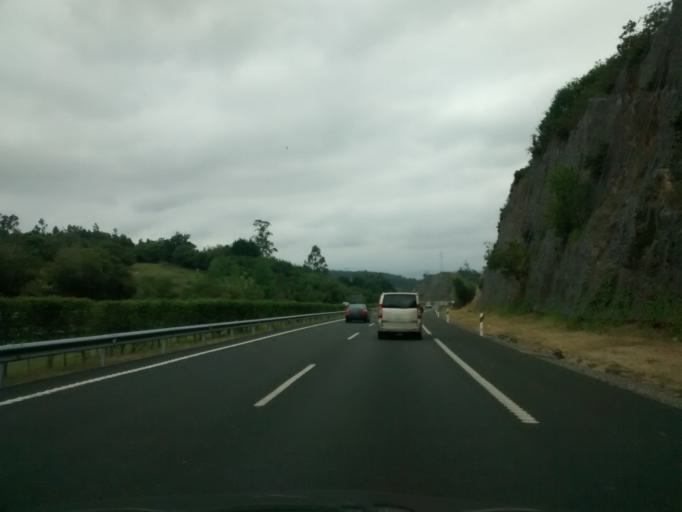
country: ES
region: Cantabria
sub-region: Provincia de Cantabria
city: Reocin
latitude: 43.3403
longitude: -4.1484
